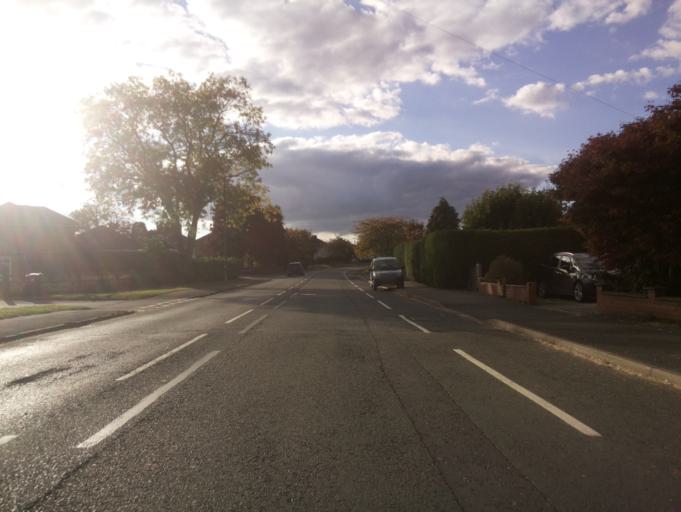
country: GB
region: England
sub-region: Herefordshire
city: Hereford
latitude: 52.0587
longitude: -2.6860
